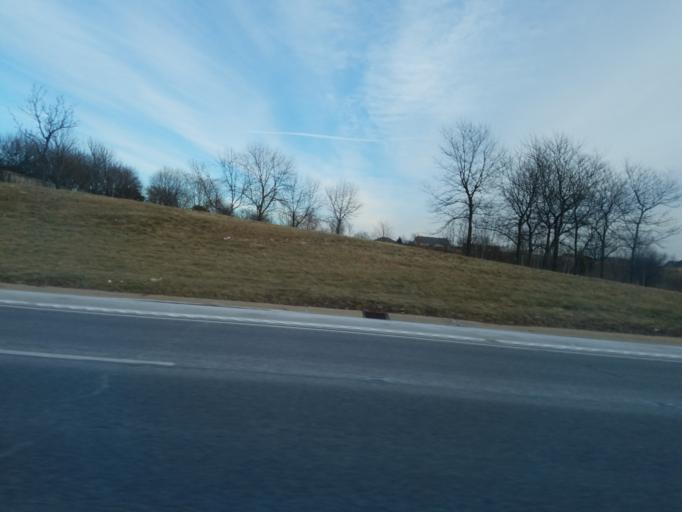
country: US
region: Illinois
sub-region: DuPage County
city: Woodridge
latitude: 41.7429
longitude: -88.0349
